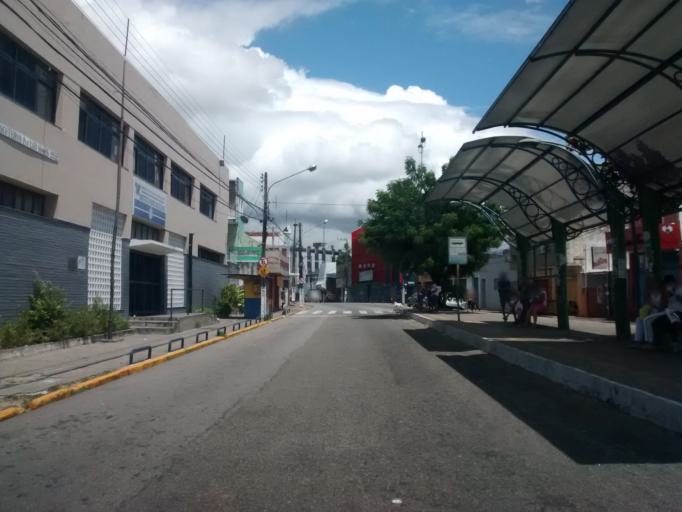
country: BR
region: Rio Grande do Norte
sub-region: Natal
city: Natal
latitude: -5.7932
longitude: -35.2144
